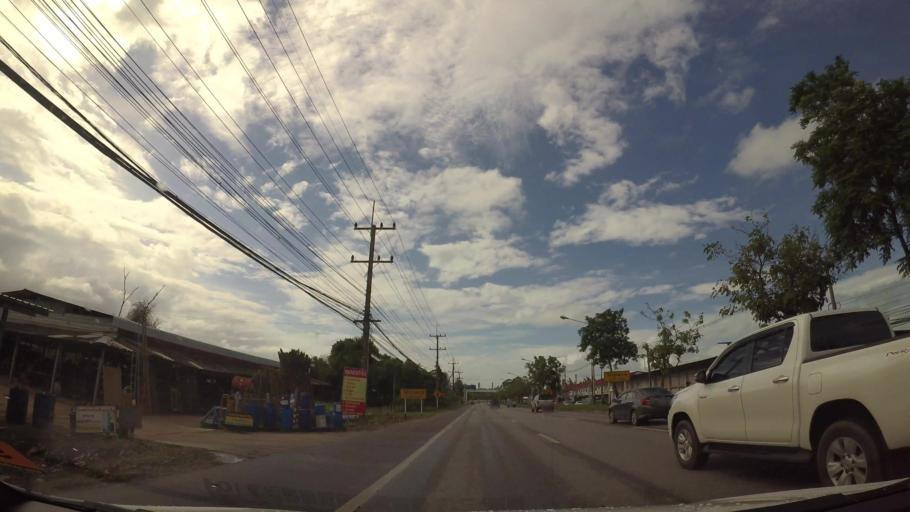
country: TH
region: Rayong
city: Rayong
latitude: 12.6673
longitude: 101.2966
